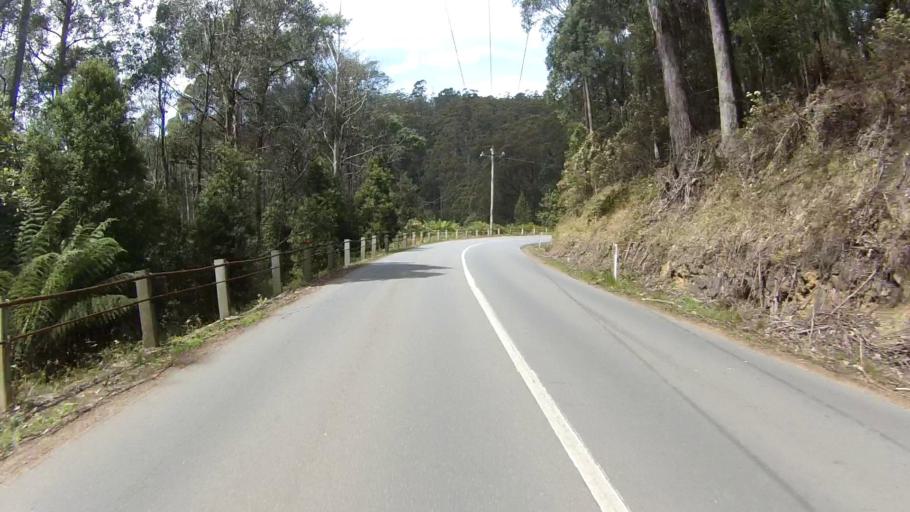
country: AU
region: Tasmania
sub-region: Kingborough
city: Kettering
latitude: -43.1257
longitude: 147.1789
